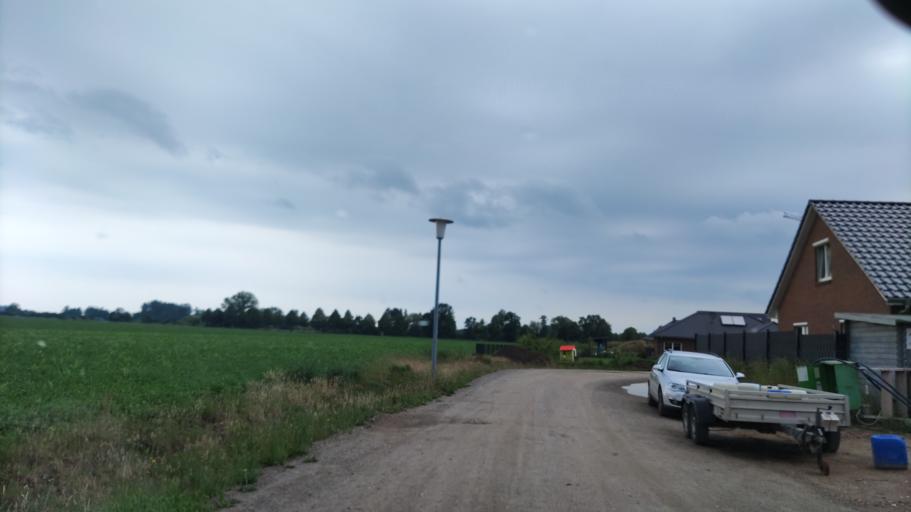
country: DE
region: Lower Saxony
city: Bleckede
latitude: 53.2856
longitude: 10.7213
